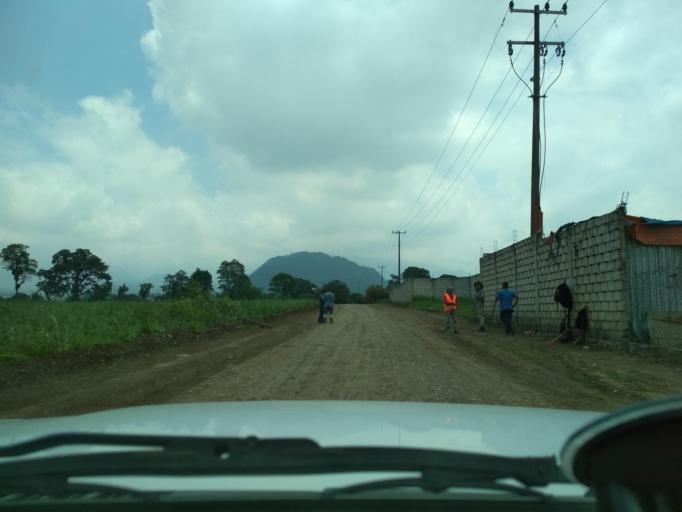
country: MX
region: Veracruz
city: Atzacan
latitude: 18.8803
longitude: -97.0791
